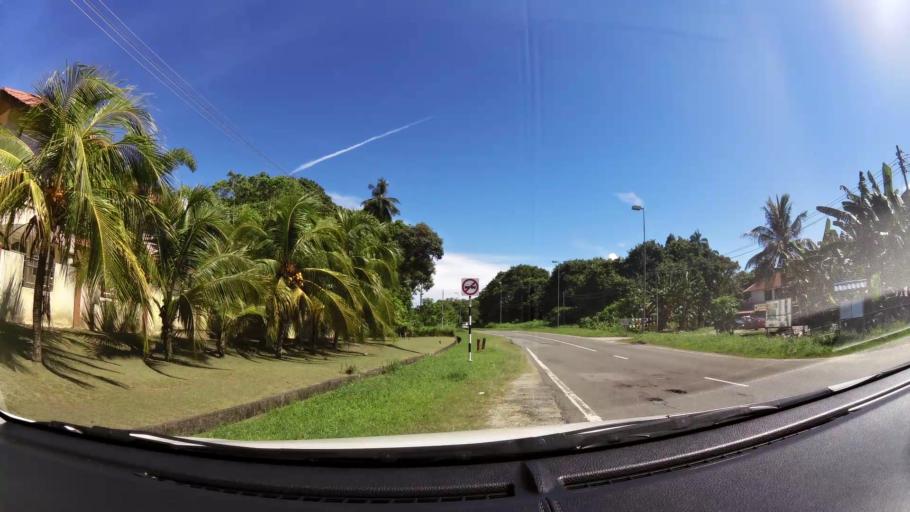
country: BN
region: Brunei and Muara
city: Bandar Seri Begawan
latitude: 5.0122
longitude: 115.0586
